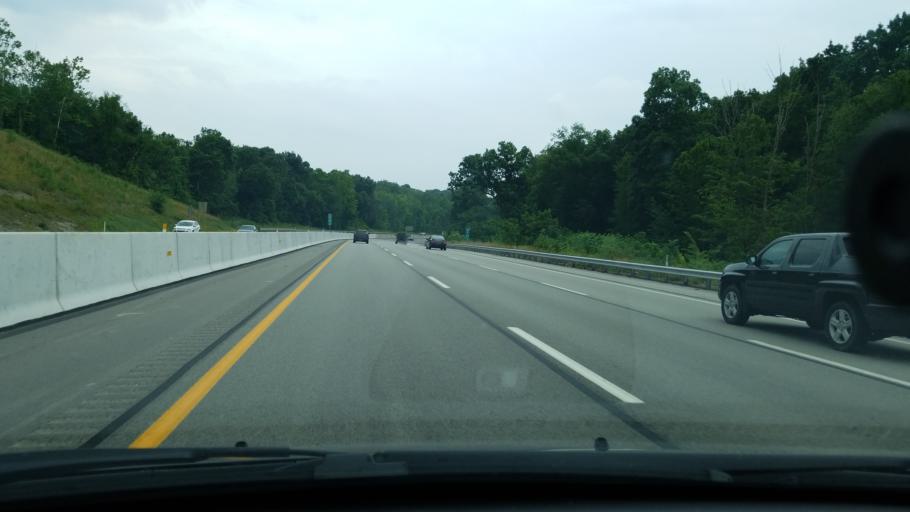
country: US
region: Pennsylvania
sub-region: Allegheny County
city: Cheswick
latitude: 40.5512
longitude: -79.8292
